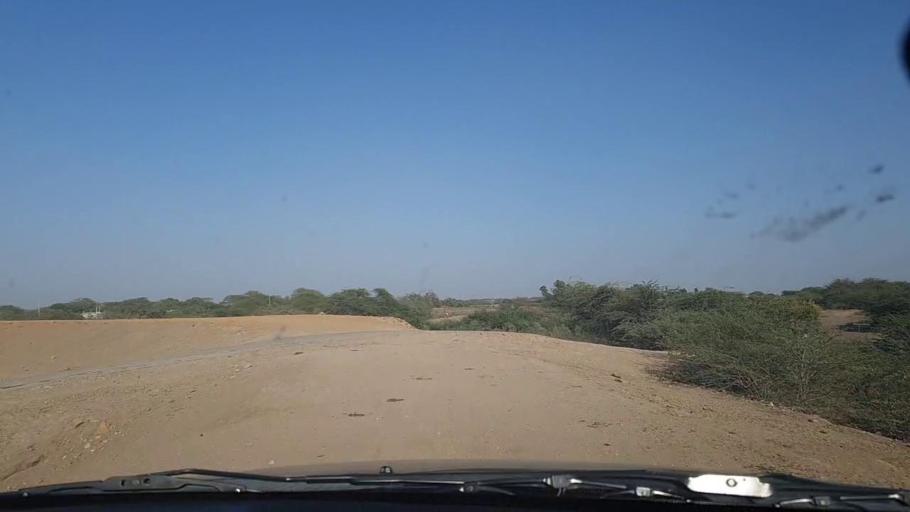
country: PK
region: Sindh
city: Chuhar Jamali
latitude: 24.3664
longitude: 67.7784
